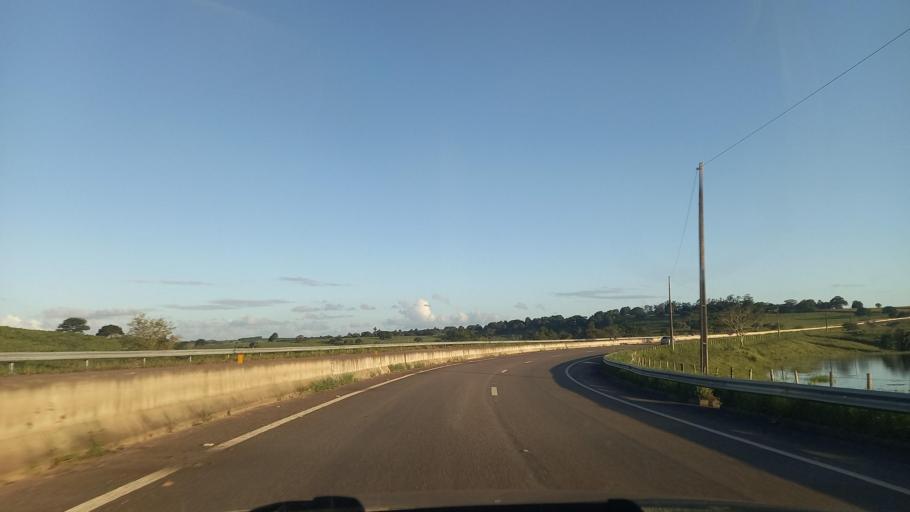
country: BR
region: Alagoas
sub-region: Limoeiro De Anadia
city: Limoeiro de Anadia
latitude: -9.7540
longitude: -36.5029
